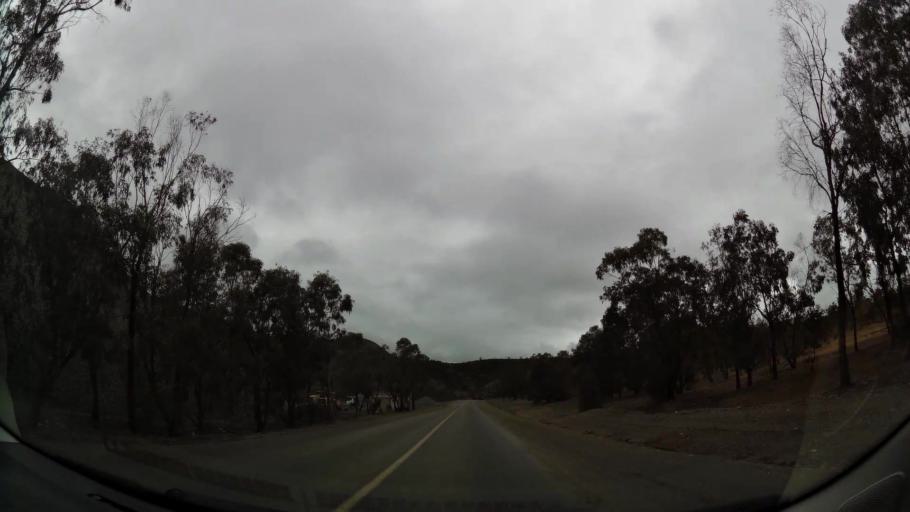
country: MA
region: Taza-Al Hoceima-Taounate
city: Imzourene
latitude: 34.9422
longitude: -3.8087
